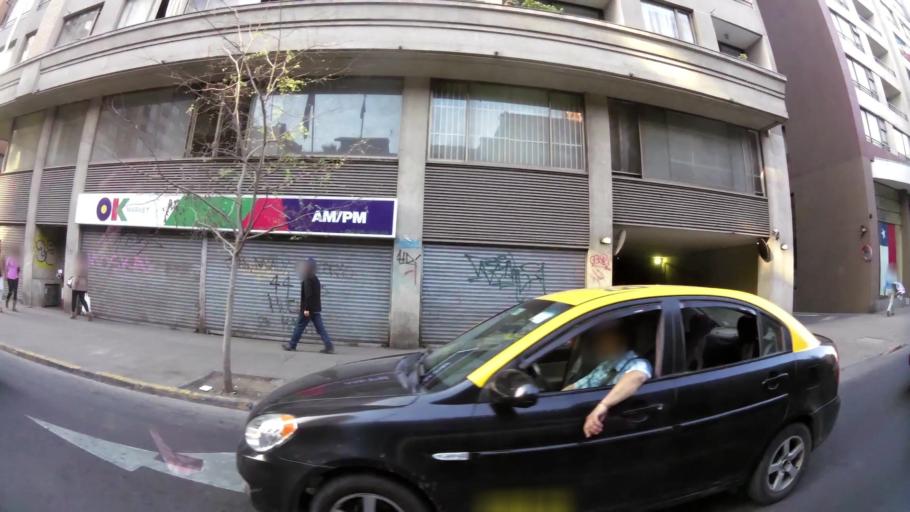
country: CL
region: Santiago Metropolitan
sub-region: Provincia de Santiago
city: Santiago
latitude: -33.4364
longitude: -70.6539
